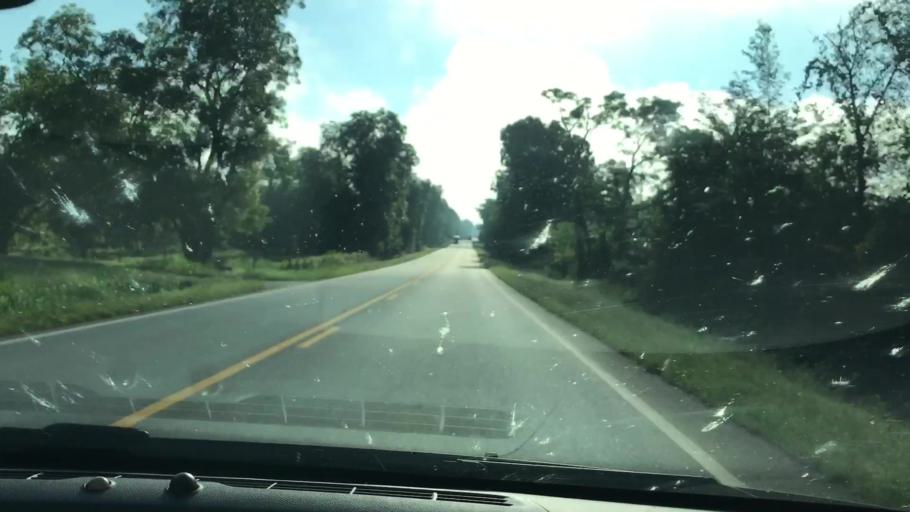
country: US
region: Georgia
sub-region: Terrell County
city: Dawson
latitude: 31.7696
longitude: -84.4769
